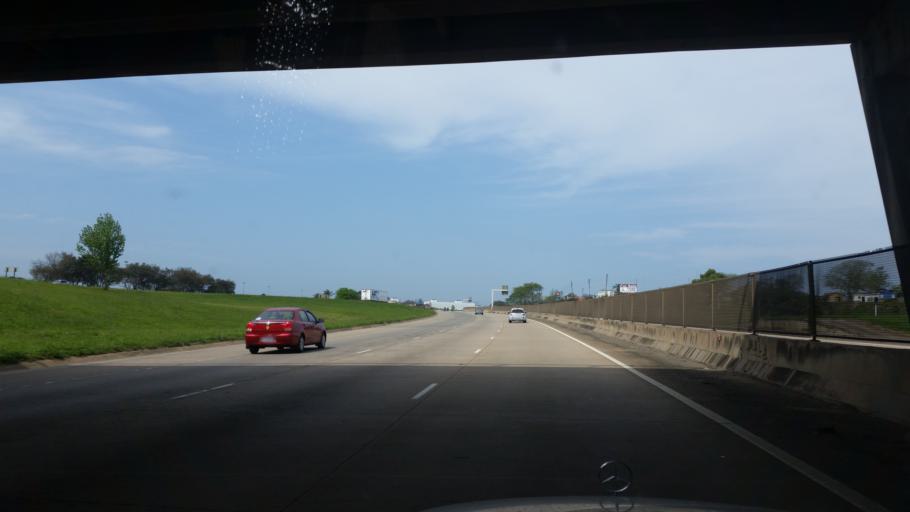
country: ZA
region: KwaZulu-Natal
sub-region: uMgungundlovu District Municipality
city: Camperdown
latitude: -29.7344
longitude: 30.5832
